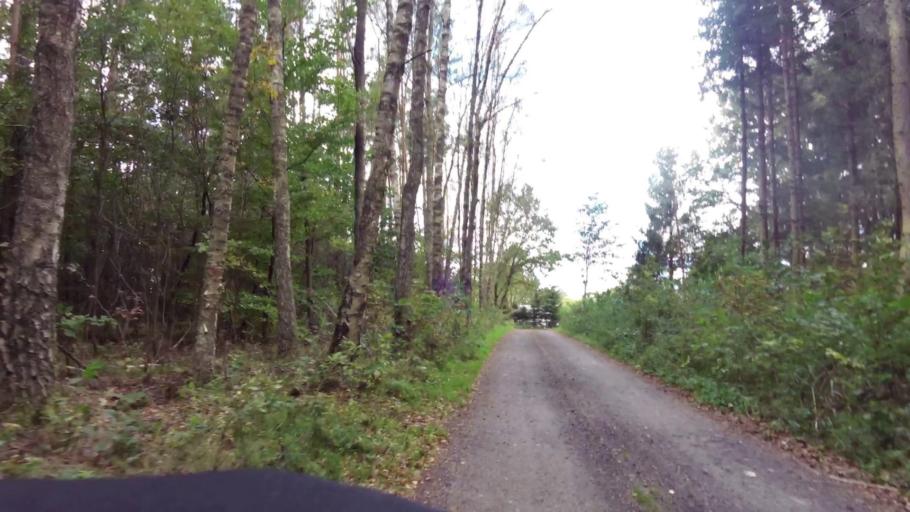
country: PL
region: West Pomeranian Voivodeship
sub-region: Powiat bialogardzki
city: Bialogard
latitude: 54.0614
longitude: 16.1137
